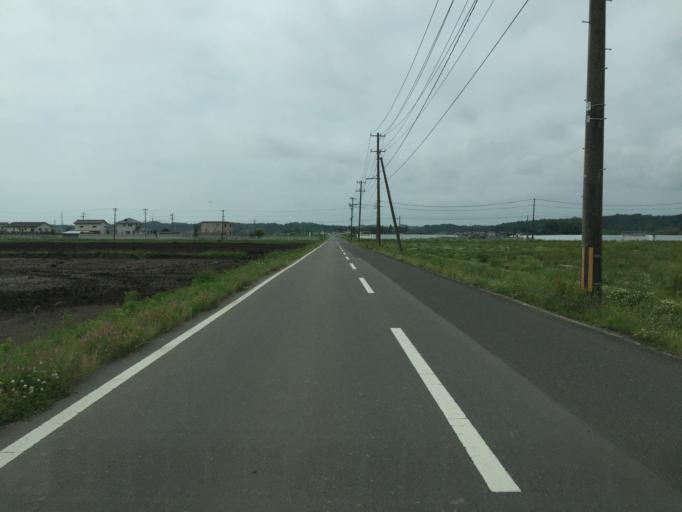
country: JP
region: Fukushima
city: Namie
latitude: 37.7006
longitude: 140.9841
